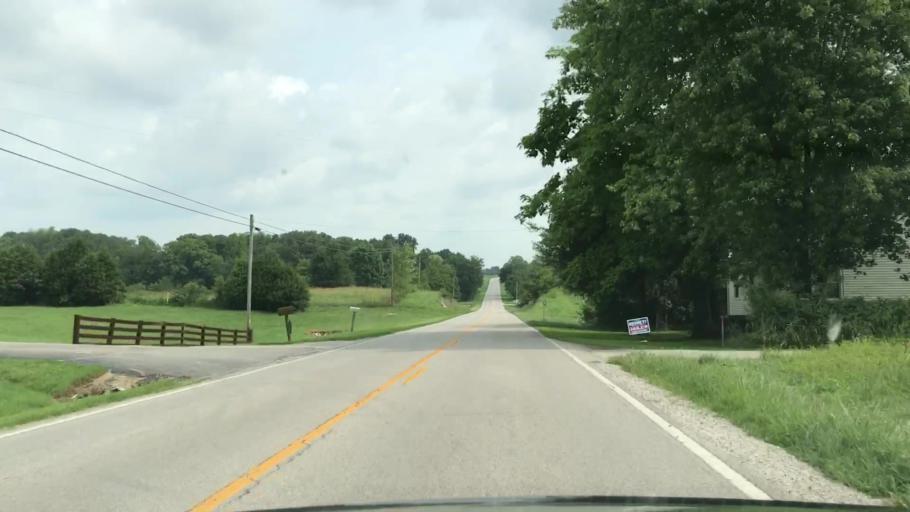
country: US
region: Kentucky
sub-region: Barren County
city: Cave City
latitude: 37.1019
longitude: -86.0037
